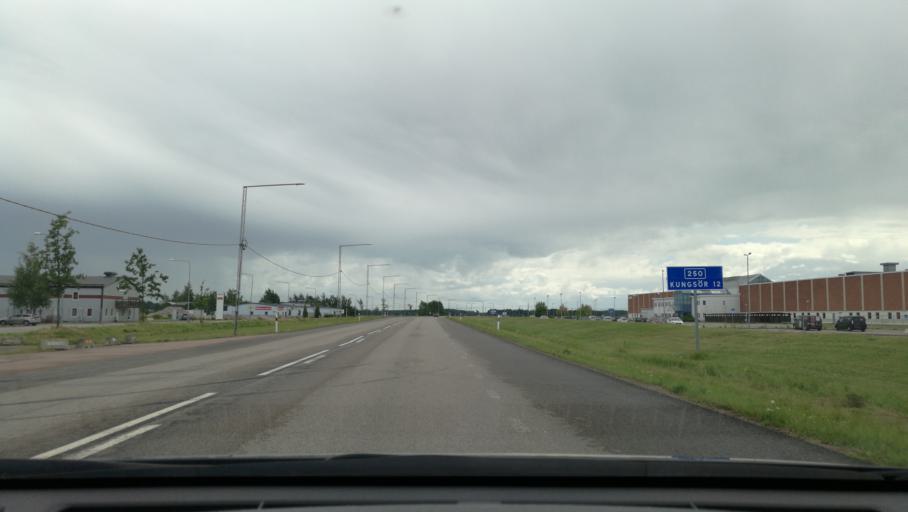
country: SE
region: Vaestmanland
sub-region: Kopings Kommun
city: Koping
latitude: 59.5016
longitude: 15.9937
